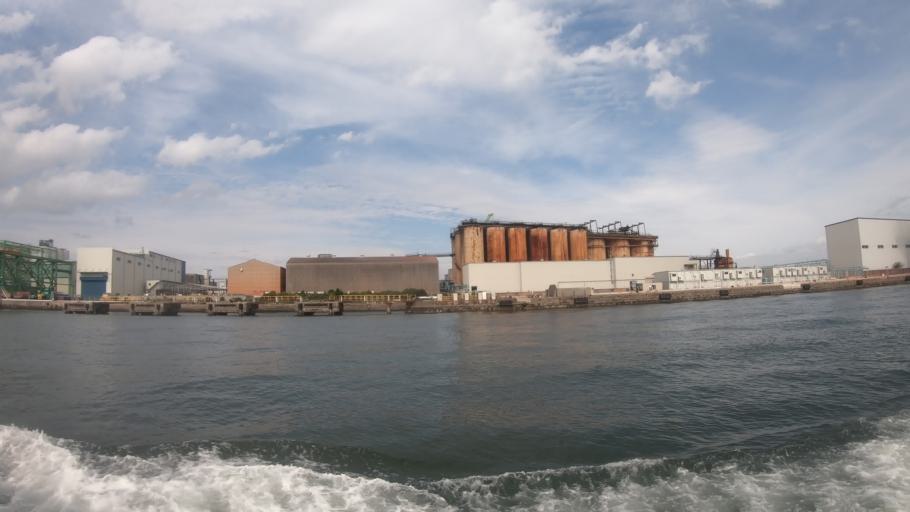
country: JP
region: Kanagawa
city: Yokohama
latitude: 35.4758
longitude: 139.6568
